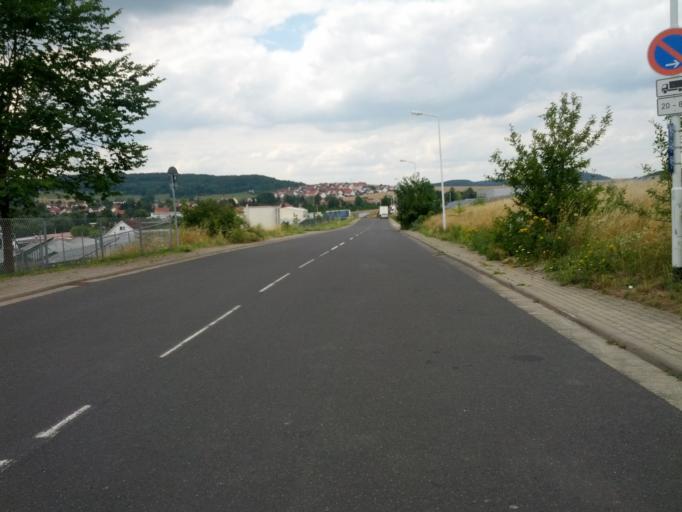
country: DE
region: Thuringia
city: Eisenach
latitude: 51.0027
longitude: 10.3270
